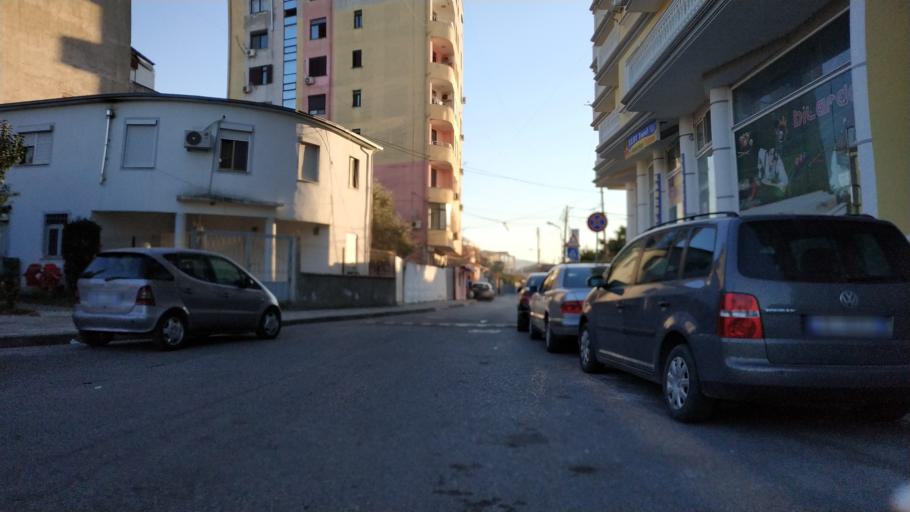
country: AL
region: Shkoder
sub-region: Rrethi i Shkodres
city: Shkoder
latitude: 42.0611
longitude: 19.5141
